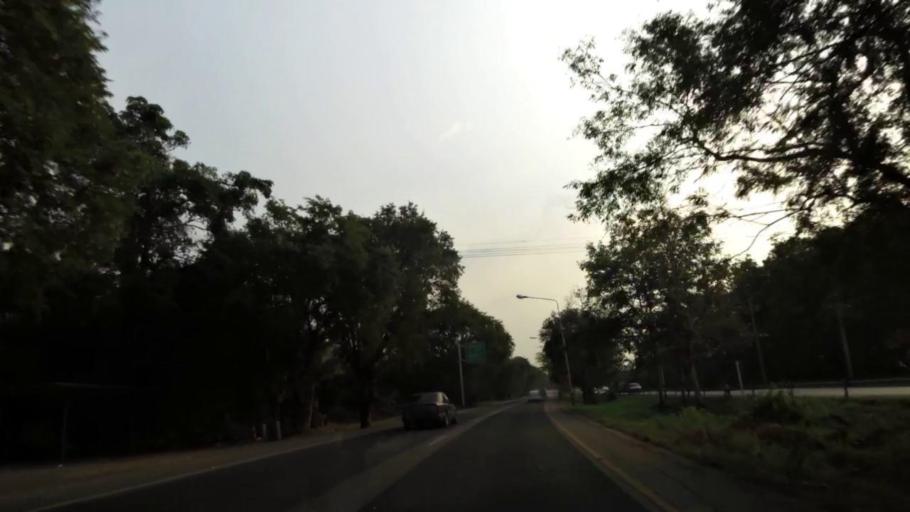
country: TH
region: Chanthaburi
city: Chanthaburi
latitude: 12.5701
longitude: 102.1624
